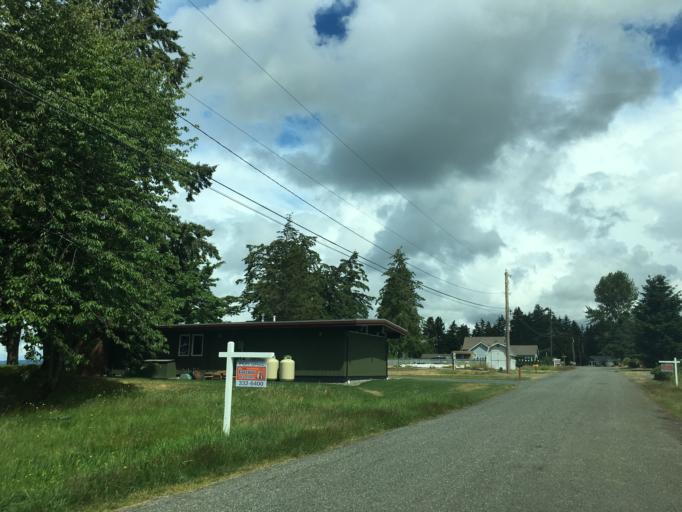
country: US
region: Washington
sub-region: Whatcom County
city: Blaine
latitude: 48.9686
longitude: -122.7330
